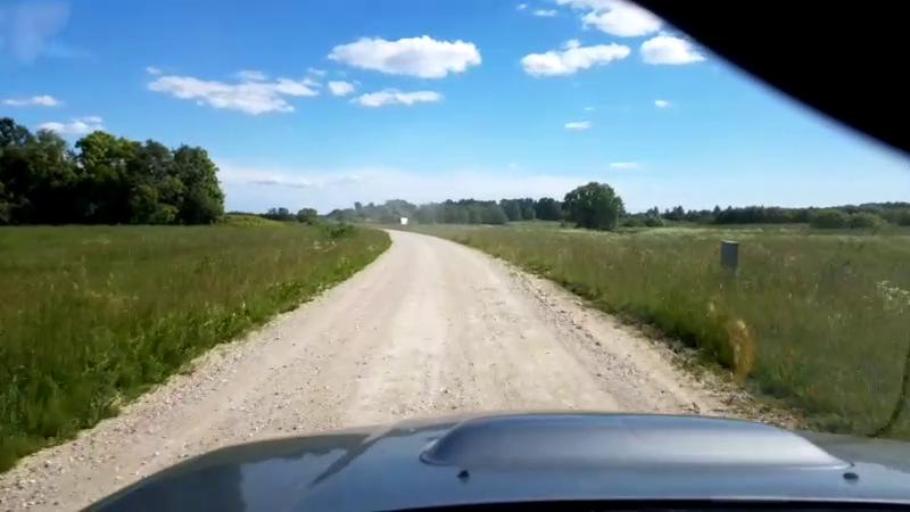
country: EE
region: Paernumaa
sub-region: Sauga vald
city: Sauga
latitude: 58.5091
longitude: 24.5158
